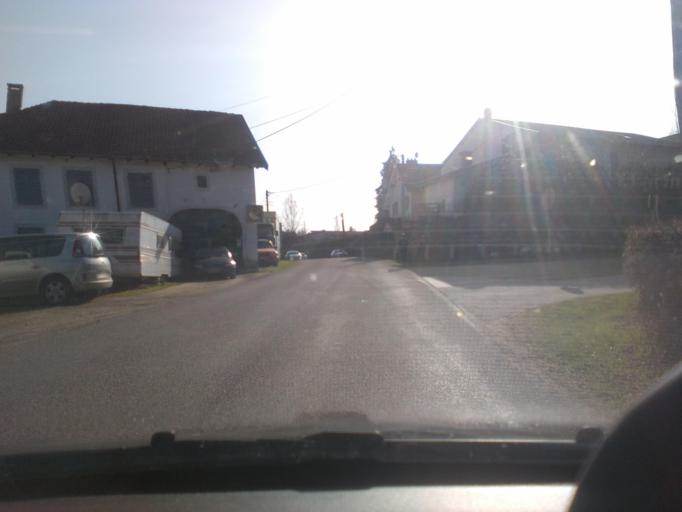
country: FR
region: Lorraine
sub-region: Departement des Vosges
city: Sainte-Marguerite
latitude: 48.2853
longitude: 6.9872
